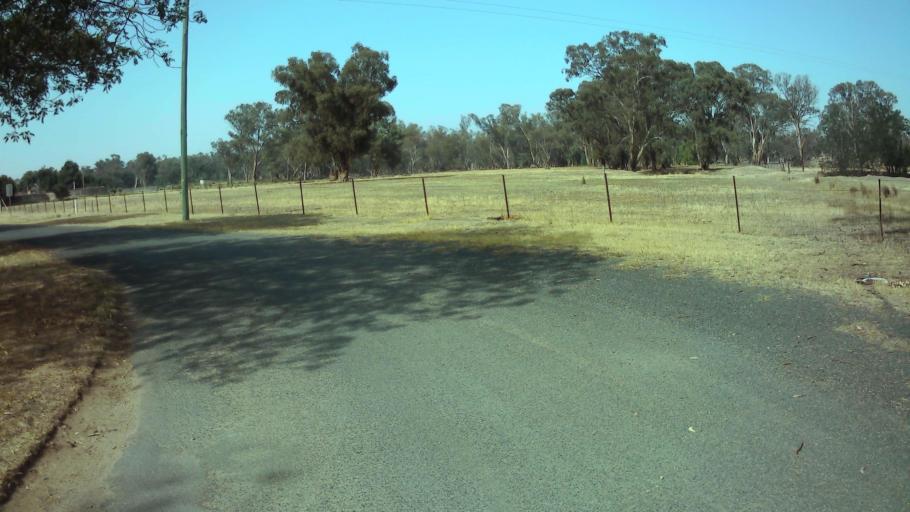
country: AU
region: New South Wales
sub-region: Weddin
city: Grenfell
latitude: -33.9000
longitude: 148.1478
